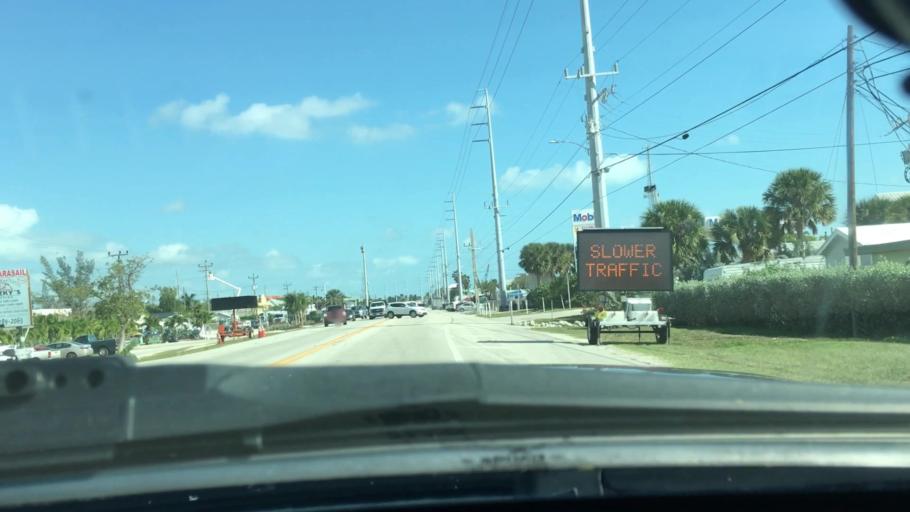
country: US
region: Florida
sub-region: Monroe County
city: Marathon
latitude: 24.7083
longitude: -81.1102
